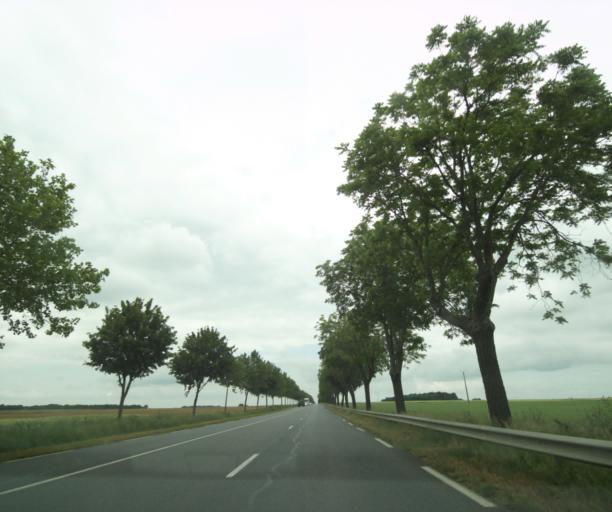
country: FR
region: Poitou-Charentes
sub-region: Departement des Deux-Sevres
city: Saint-Jean-de-Thouars
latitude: 46.9344
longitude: -0.2009
